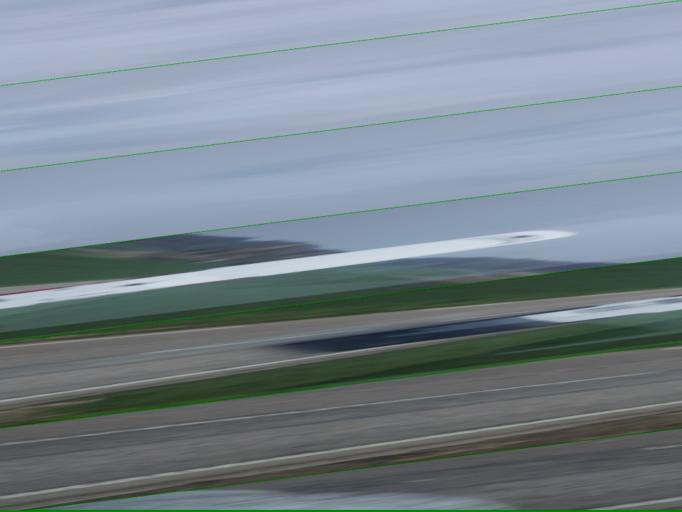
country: FR
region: Ile-de-France
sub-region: Departement des Yvelines
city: Houdan
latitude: 48.8129
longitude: 1.6011
